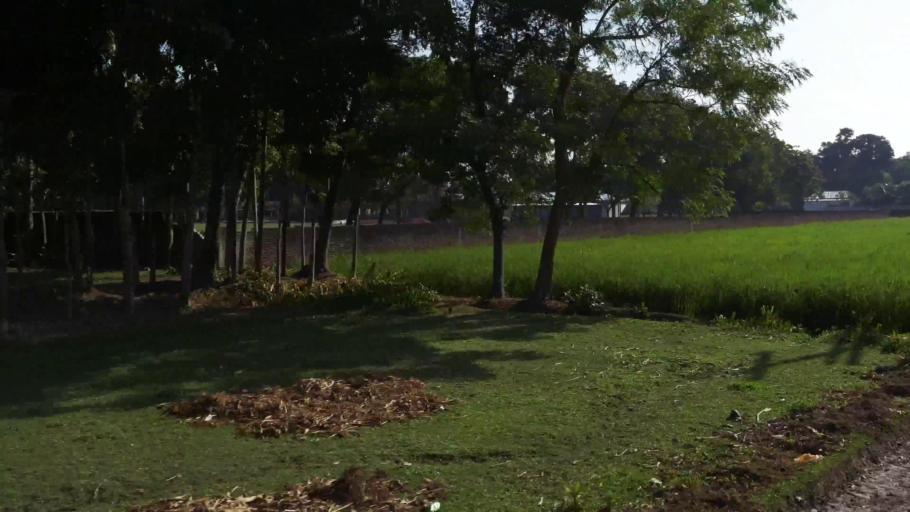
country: BD
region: Dhaka
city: Muktagacha
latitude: 24.8135
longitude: 90.2883
